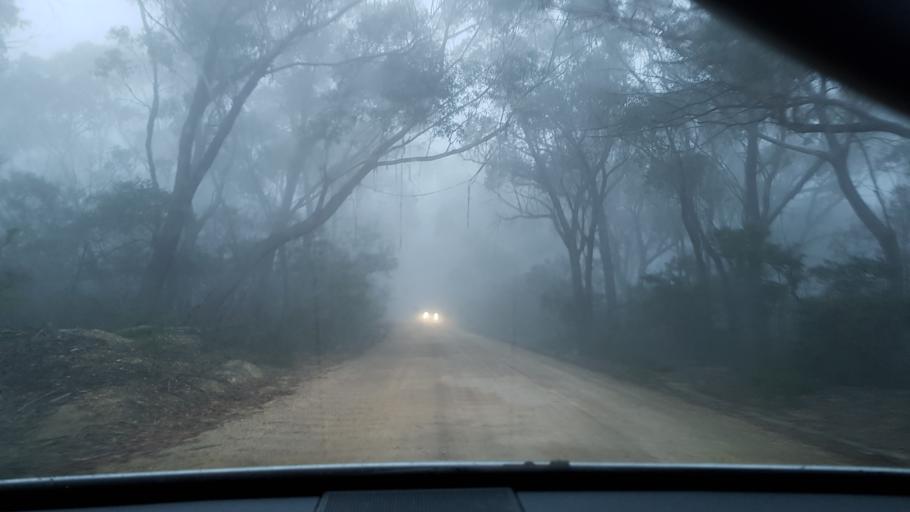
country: AU
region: New South Wales
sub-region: Blue Mountains Municipality
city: Katoomba
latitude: -33.9901
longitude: 150.1052
